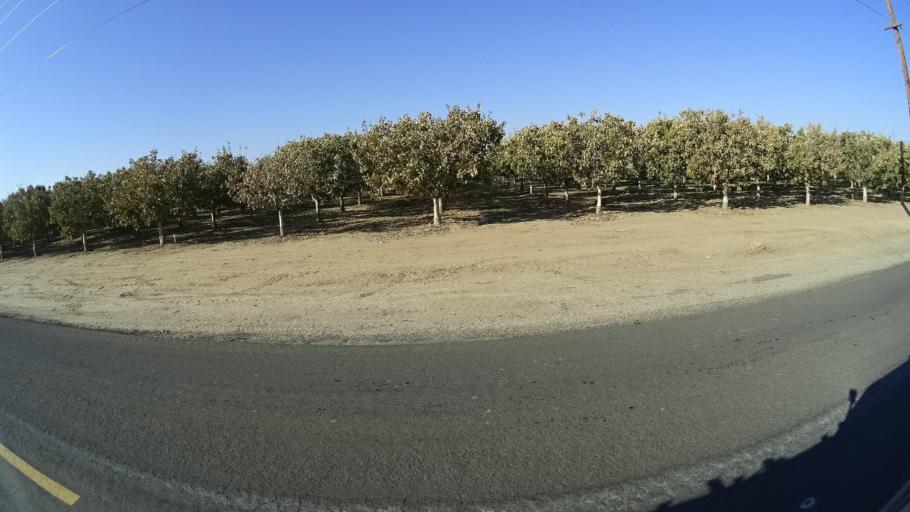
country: US
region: California
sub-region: Tulare County
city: Richgrove
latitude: 35.7438
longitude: -119.1342
